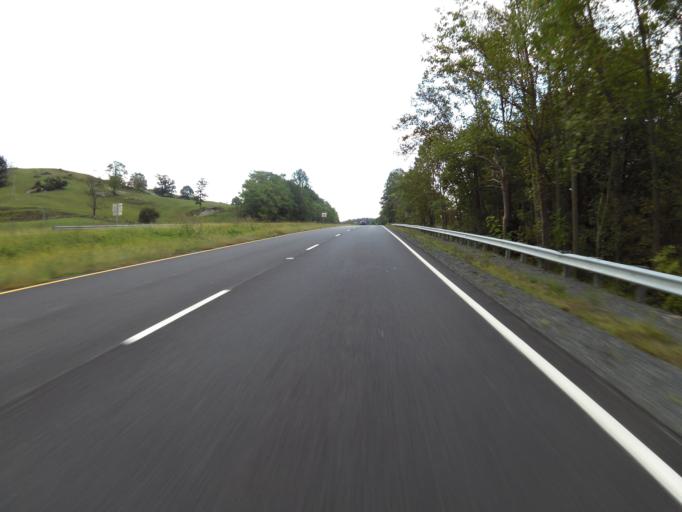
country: US
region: Virginia
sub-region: Rappahannock County
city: Washington
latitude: 38.7237
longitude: -78.1122
